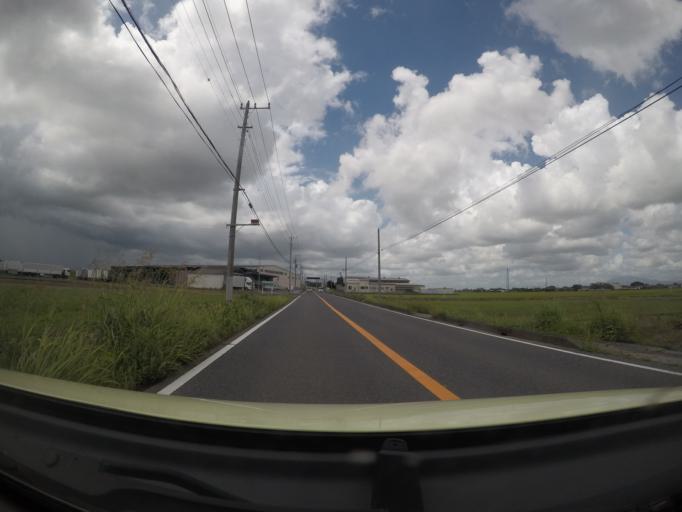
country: JP
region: Ibaraki
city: Mitsukaido
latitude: 36.0562
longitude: 139.9832
